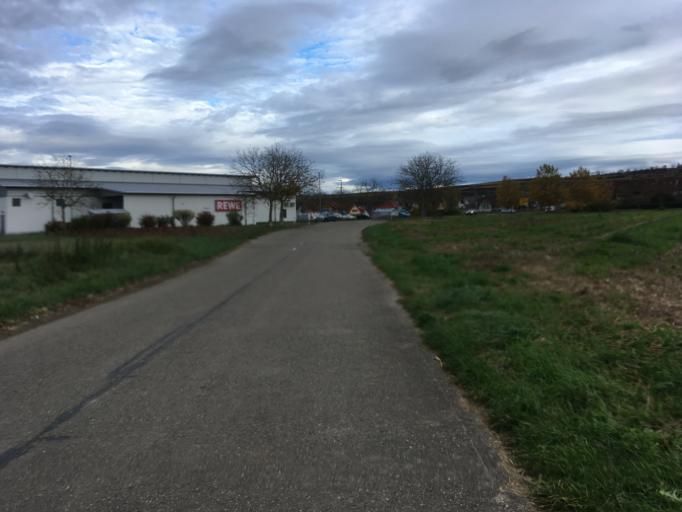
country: DE
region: Baden-Wuerttemberg
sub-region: Freiburg Region
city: Merdingen
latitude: 48.0195
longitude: 7.6799
